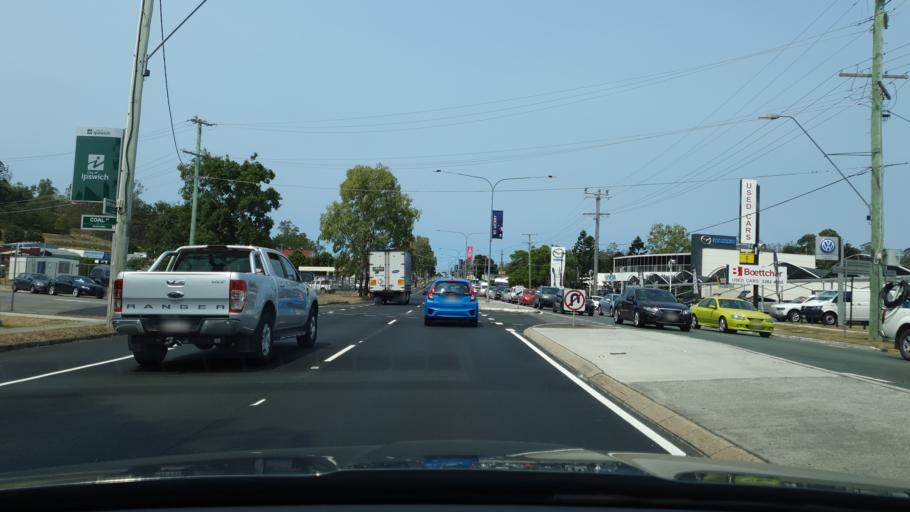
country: AU
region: Queensland
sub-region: Ipswich
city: Bundamba
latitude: -27.6099
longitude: 152.8074
